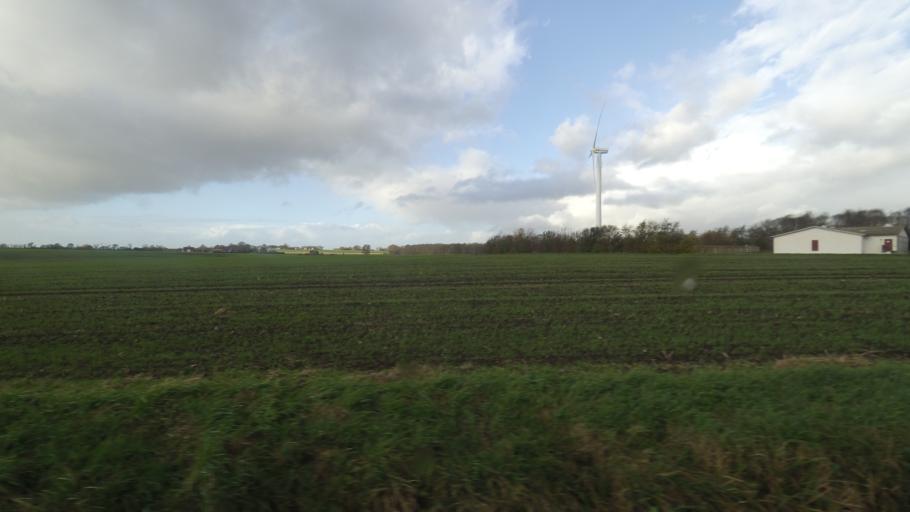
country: DK
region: Central Jutland
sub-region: Odder Kommune
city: Odder
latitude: 55.9038
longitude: 10.1979
